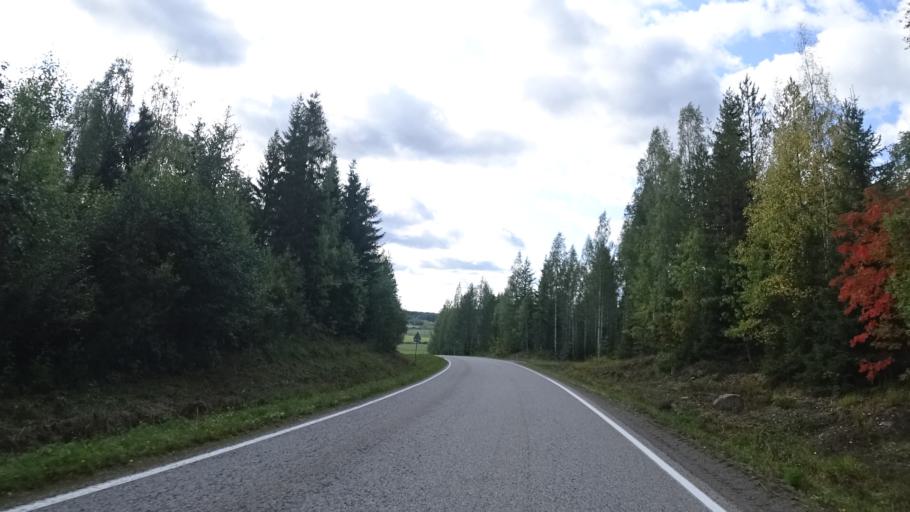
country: RU
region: Republic of Karelia
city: Vyartsilya
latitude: 62.2224
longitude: 30.6380
